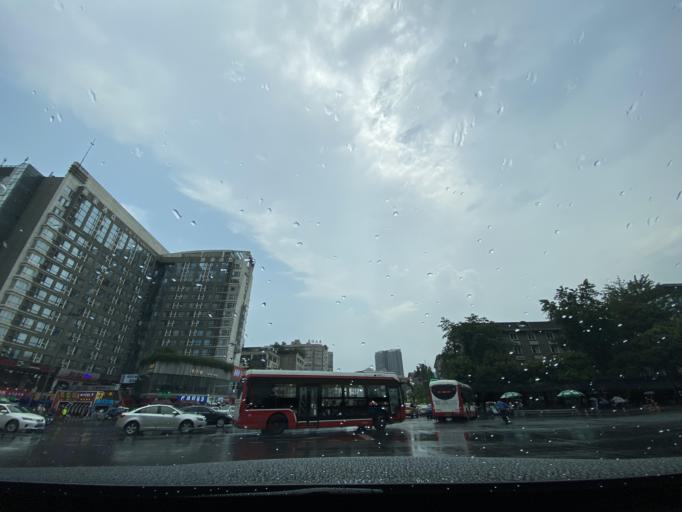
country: CN
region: Sichuan
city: Chengdu
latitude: 30.6550
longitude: 104.0759
